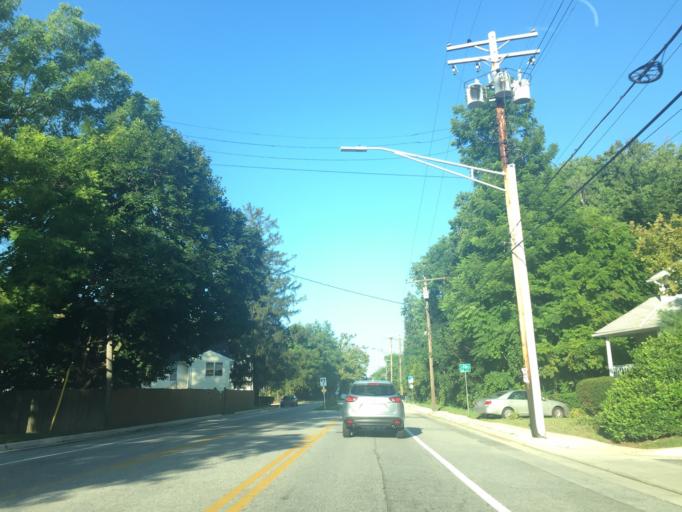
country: US
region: Maryland
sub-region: Baltimore County
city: Catonsville
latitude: 39.2762
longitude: -76.7400
